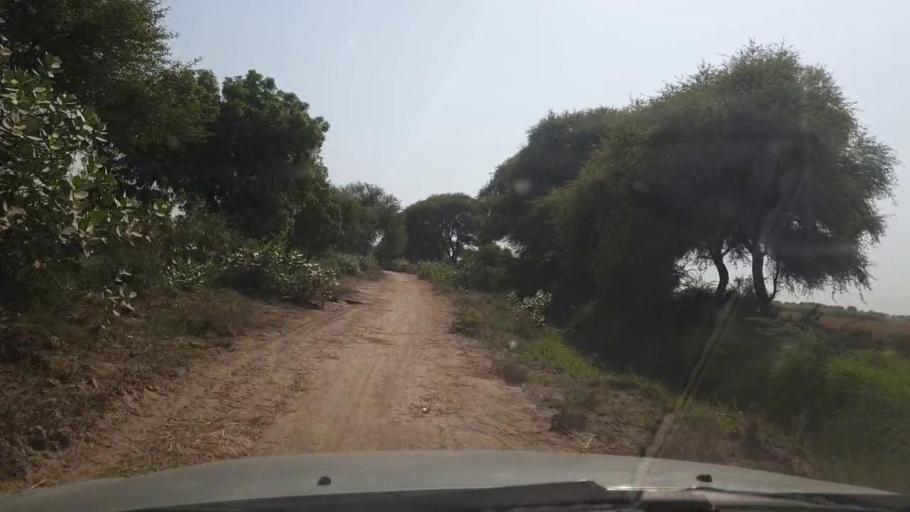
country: PK
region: Sindh
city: Bulri
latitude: 24.8680
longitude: 68.3108
